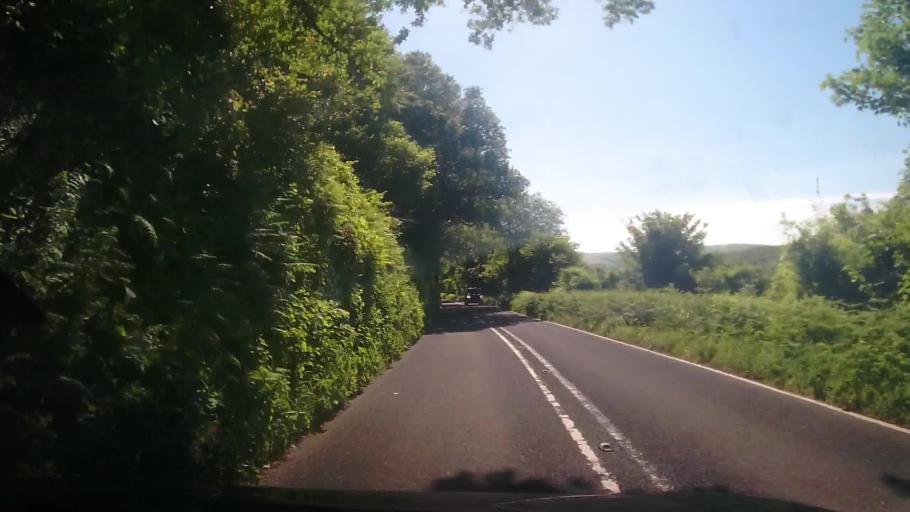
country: GB
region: England
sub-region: Devon
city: Dartmouth
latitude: 50.3684
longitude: -3.5624
